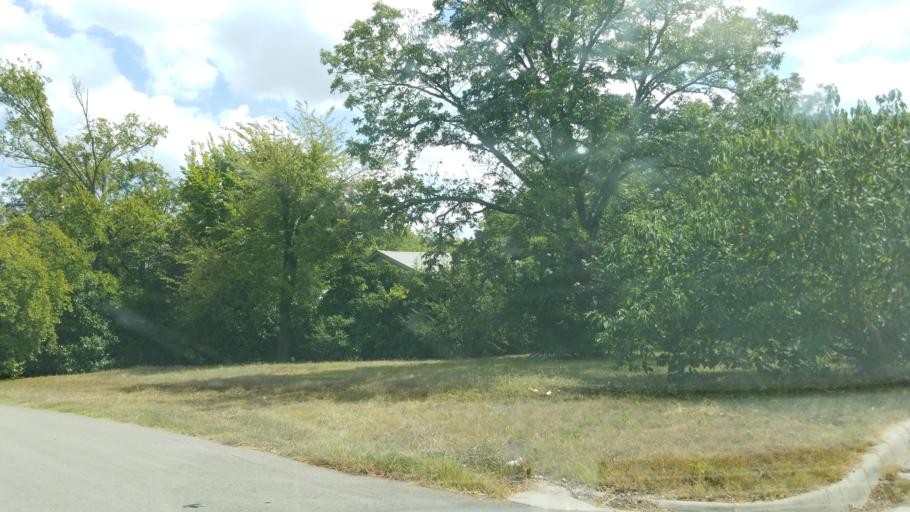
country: US
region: Texas
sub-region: Tarrant County
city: Euless
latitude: 32.8343
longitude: -97.0824
